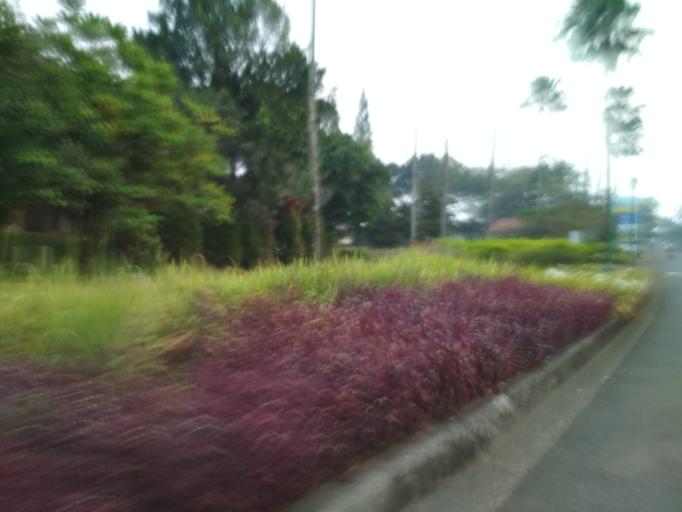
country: ID
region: West Java
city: Caringin
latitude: -6.6628
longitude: 106.8328
